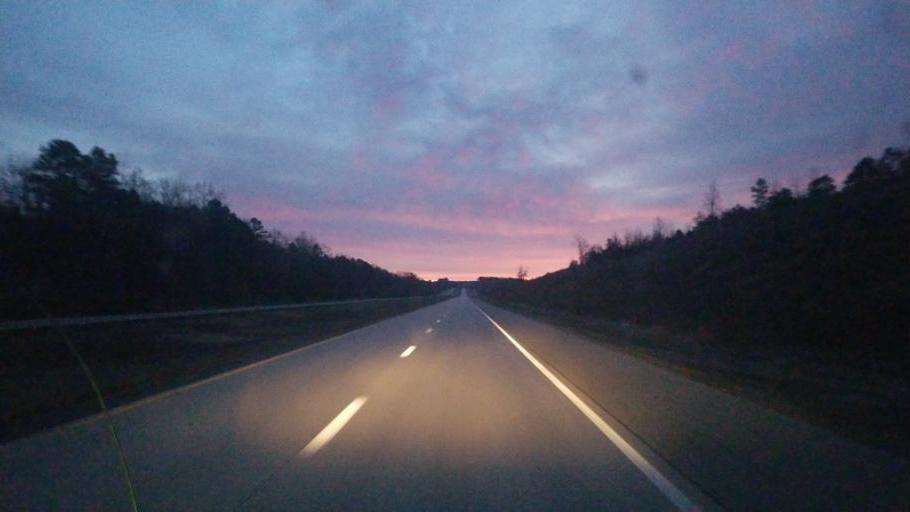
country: US
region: Missouri
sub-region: Shannon County
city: Winona
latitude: 36.9973
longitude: -91.4459
